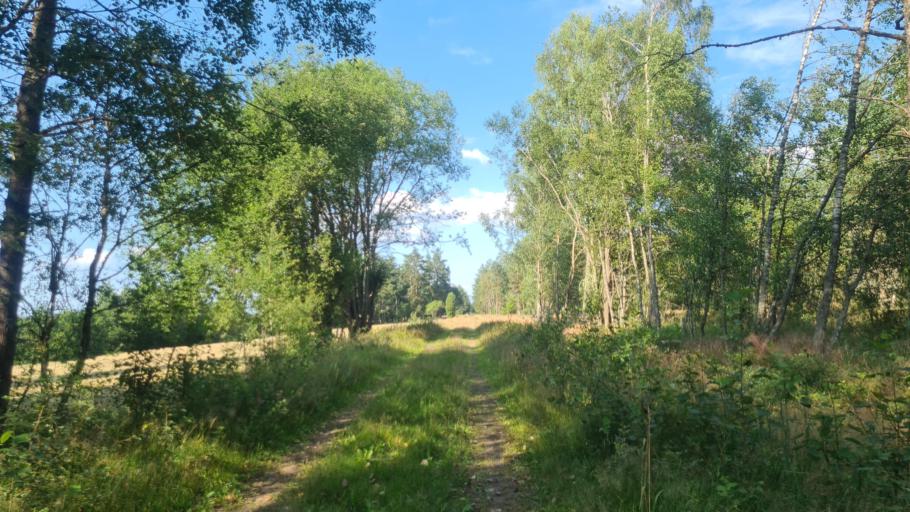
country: SE
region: Kronoberg
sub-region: Ljungby Kommun
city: Ljungby
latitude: 56.7639
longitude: 13.8925
